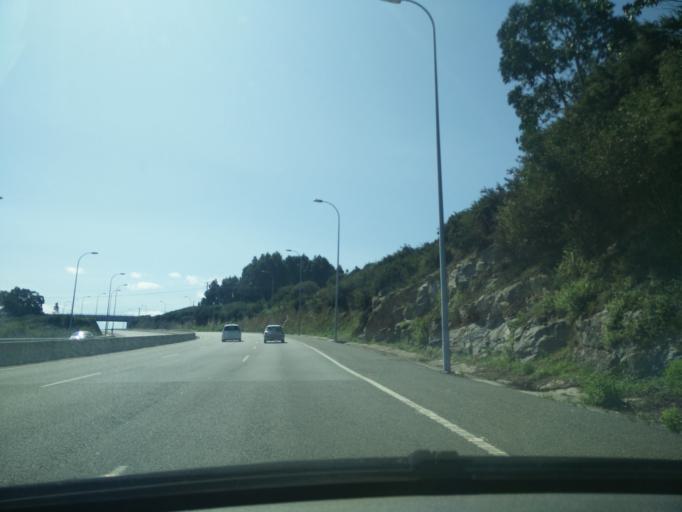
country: ES
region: Galicia
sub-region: Provincia da Coruna
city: A Coruna
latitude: 43.3635
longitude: -8.4326
